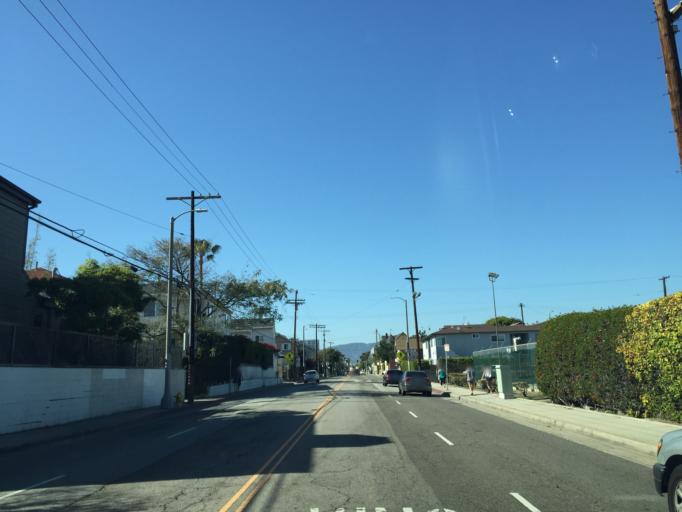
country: US
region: California
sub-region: Los Angeles County
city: Marina del Rey
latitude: 33.9934
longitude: -118.4768
